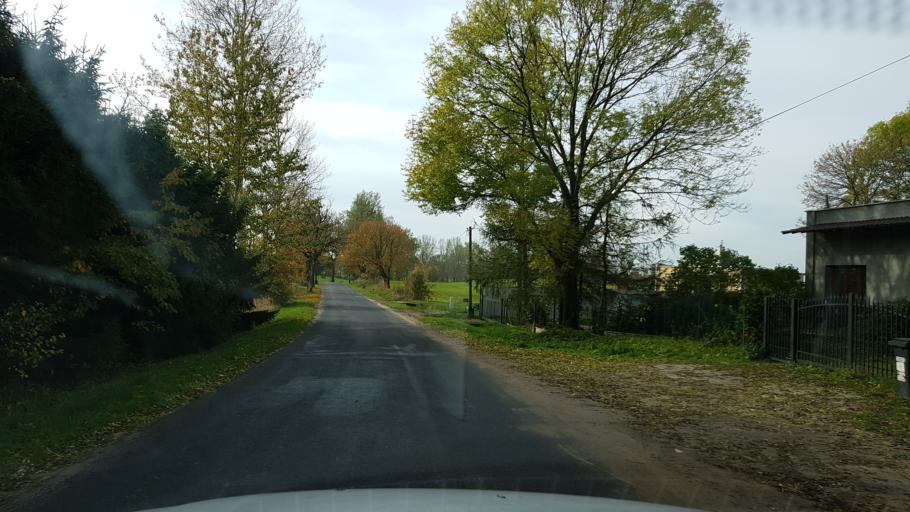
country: PL
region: West Pomeranian Voivodeship
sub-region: Powiat swidwinski
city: Polczyn-Zdroj
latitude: 53.7435
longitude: 16.0361
